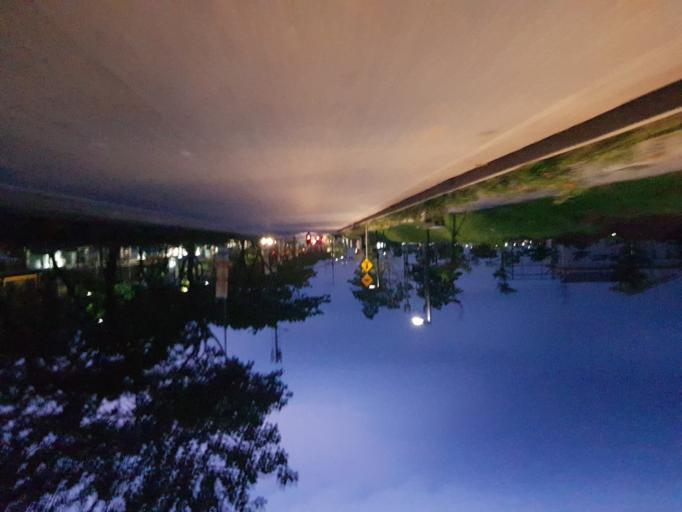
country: ID
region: West Java
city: Serpong
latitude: -6.3174
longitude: 106.6512
